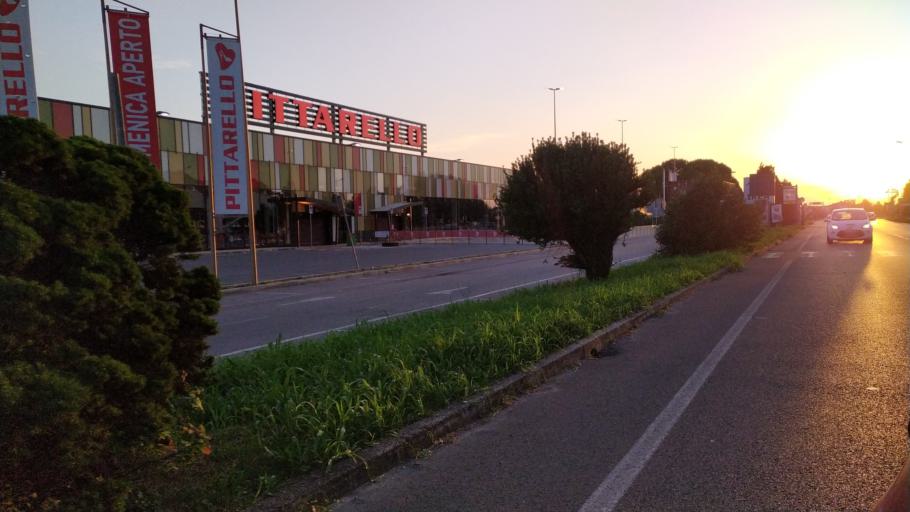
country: IT
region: Veneto
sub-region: Provincia di Padova
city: Vigonza
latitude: 45.4217
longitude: 11.9794
